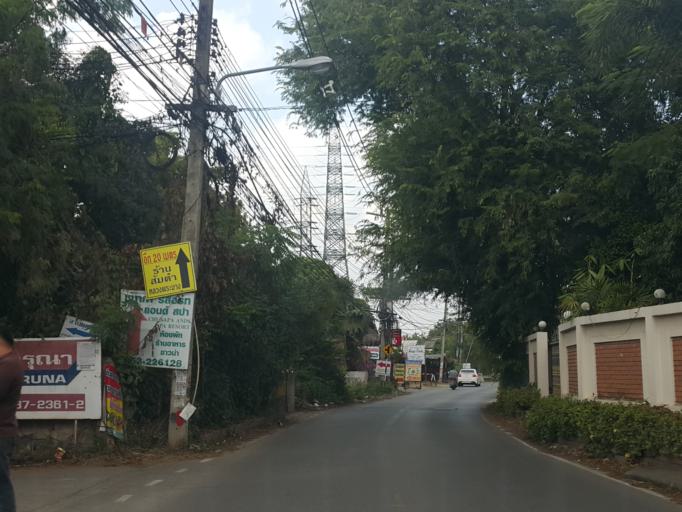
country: TH
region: Chiang Mai
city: Chiang Mai
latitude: 18.8137
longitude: 99.0013
